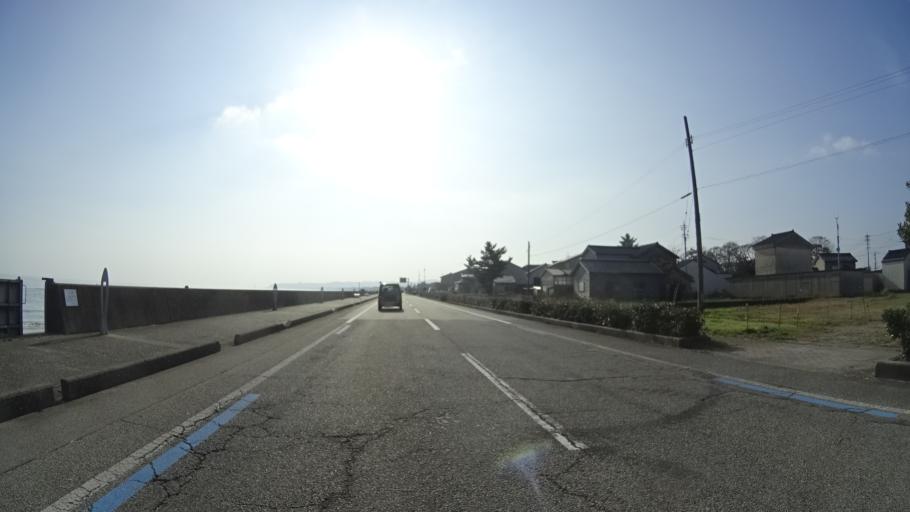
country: JP
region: Toyama
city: Himi
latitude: 36.8535
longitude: 136.9911
